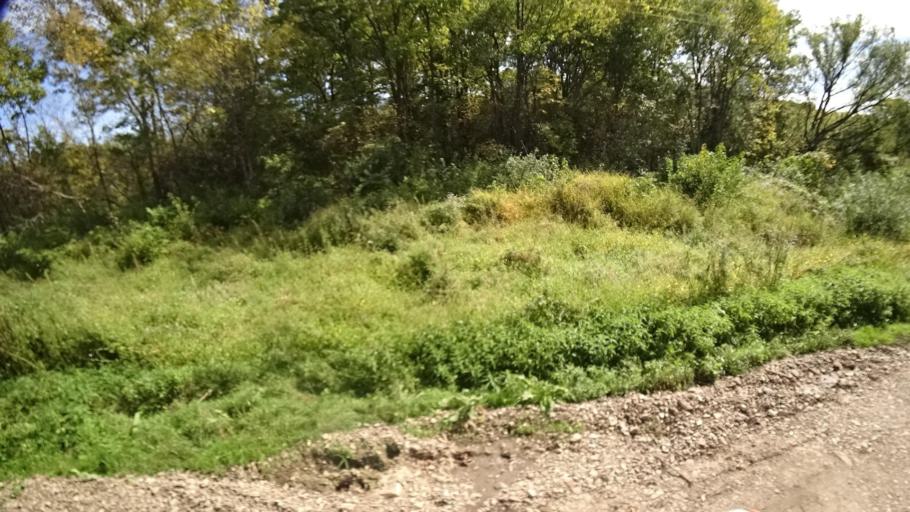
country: RU
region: Primorskiy
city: Kirovskiy
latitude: 44.7570
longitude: 133.6115
